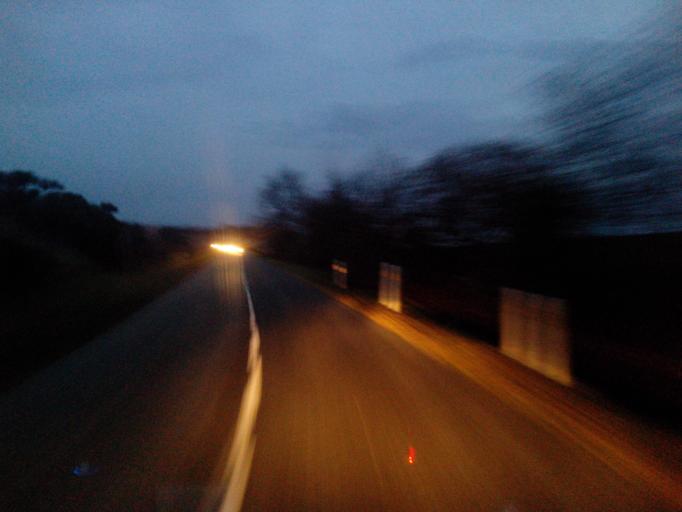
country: FR
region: Languedoc-Roussillon
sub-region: Departement de l'Aude
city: Villeneuve-la-Comptal
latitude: 43.2814
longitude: 1.8497
